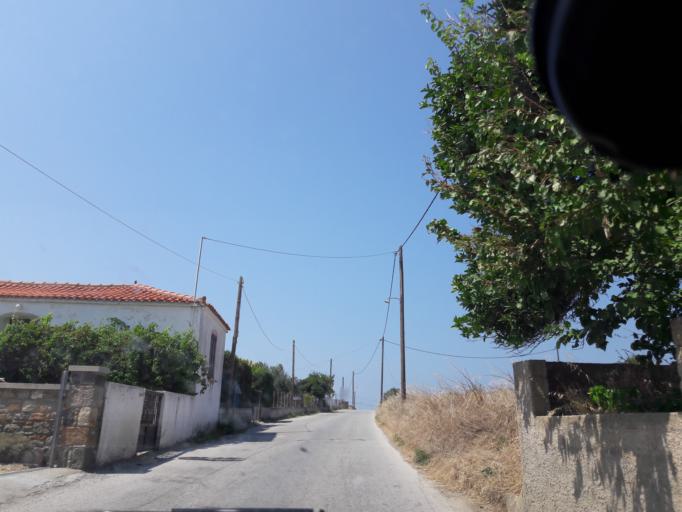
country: GR
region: North Aegean
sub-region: Nomos Lesvou
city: Myrina
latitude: 39.9244
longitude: 25.2992
